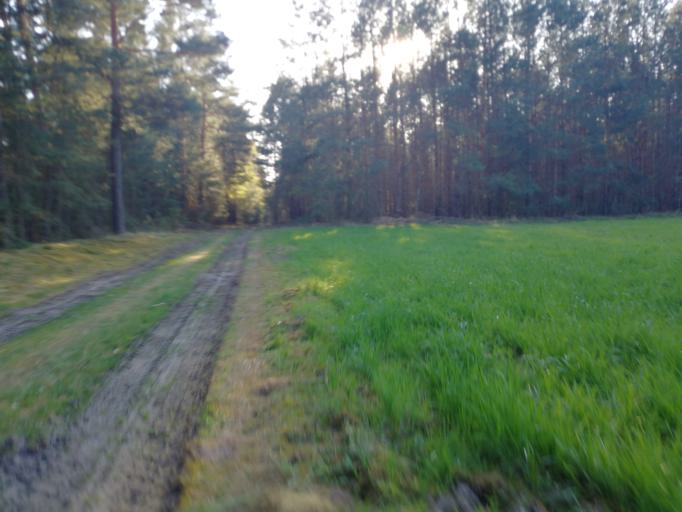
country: DE
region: Brandenburg
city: Calau
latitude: 51.7313
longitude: 14.0005
